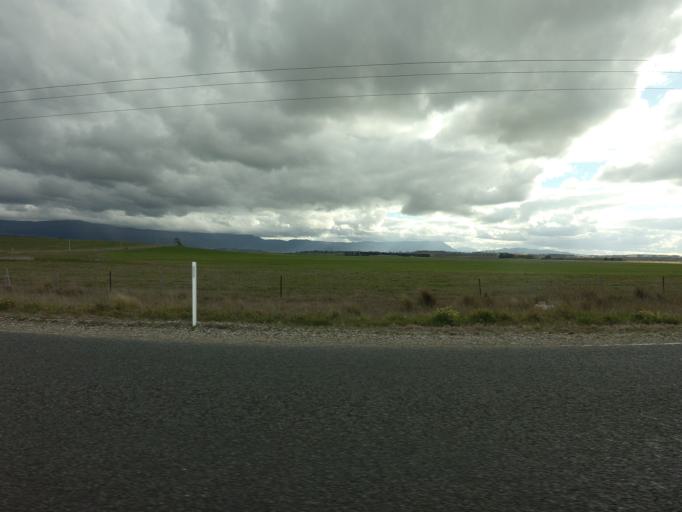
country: AU
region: Tasmania
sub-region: Northern Midlands
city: Longford
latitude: -41.7544
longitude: 147.0825
